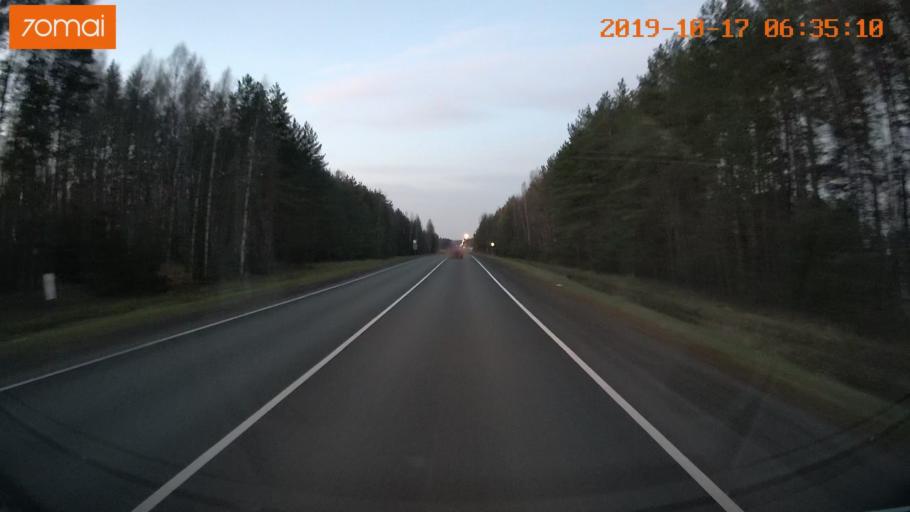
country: RU
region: Ivanovo
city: Novoye Leushino
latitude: 56.6951
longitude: 40.6259
